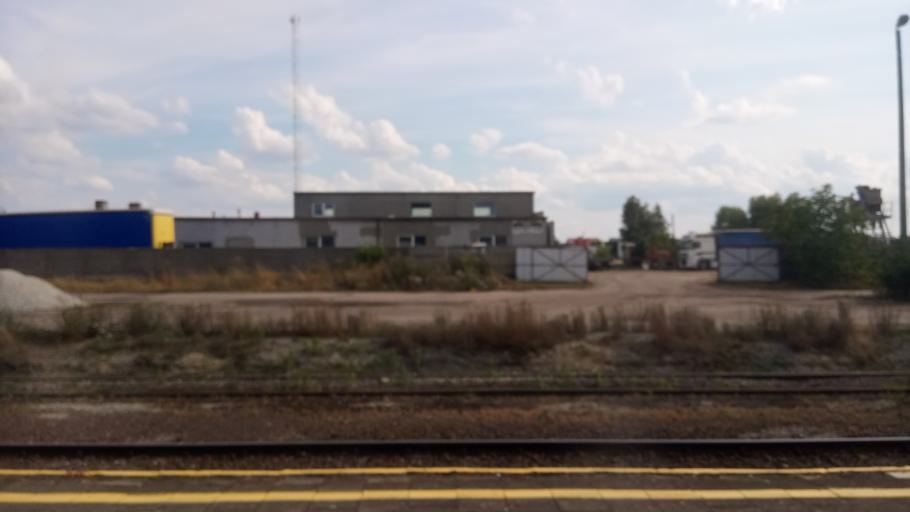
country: PL
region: Greater Poland Voivodeship
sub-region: Powiat pilski
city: Osiek nad Notecia
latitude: 53.1193
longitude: 17.2978
